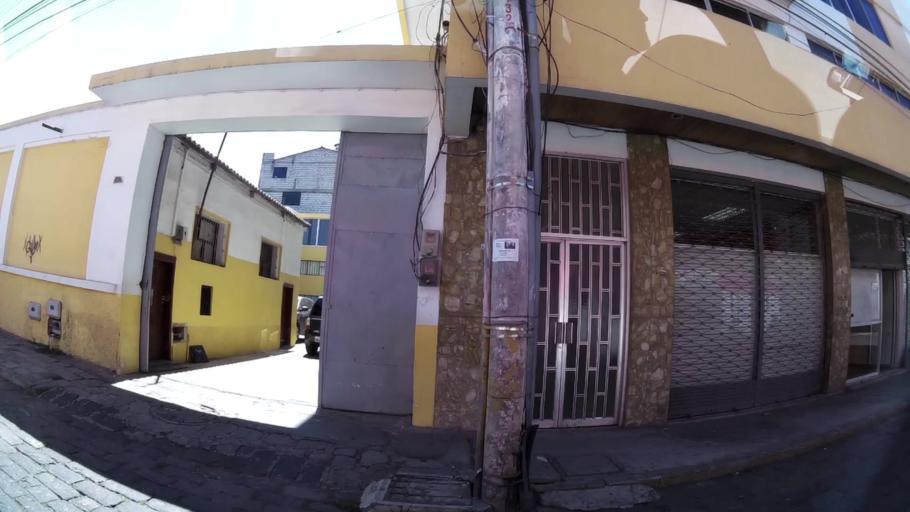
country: EC
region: Chimborazo
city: Riobamba
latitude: -1.6702
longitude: -78.6515
